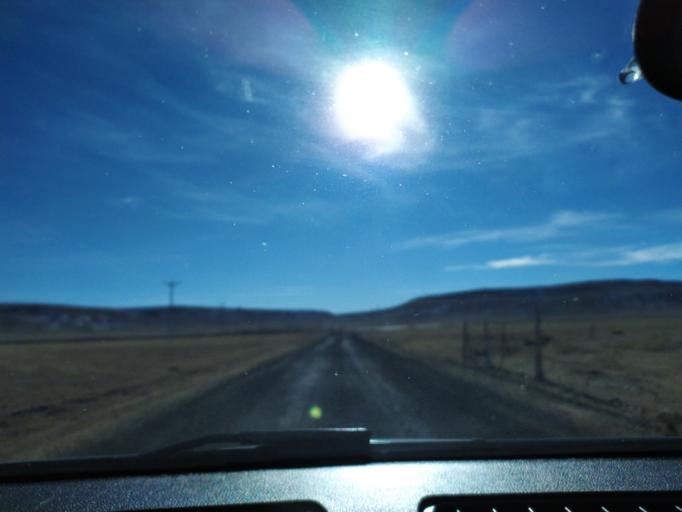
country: TR
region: Kayseri
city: Orensehir
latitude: 39.0990
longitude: 36.6987
